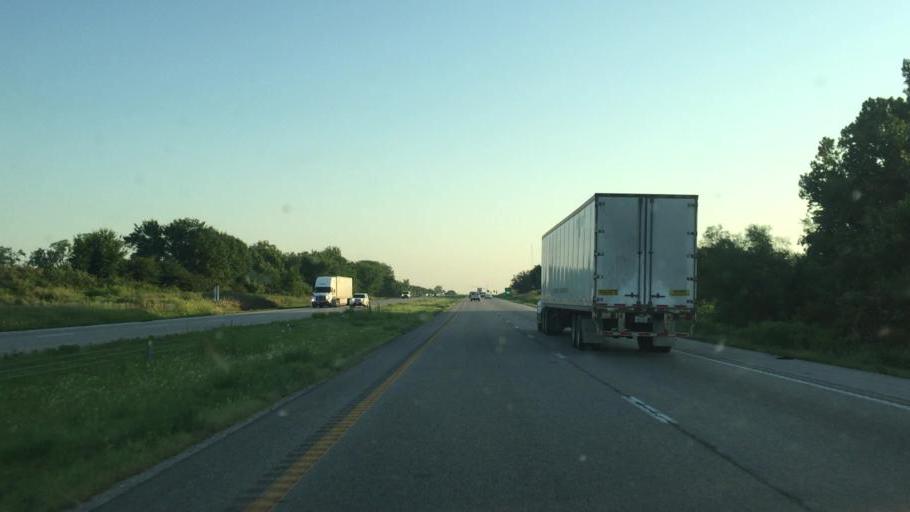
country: US
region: Missouri
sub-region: Platte County
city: Platte City
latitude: 39.4228
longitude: -94.7897
